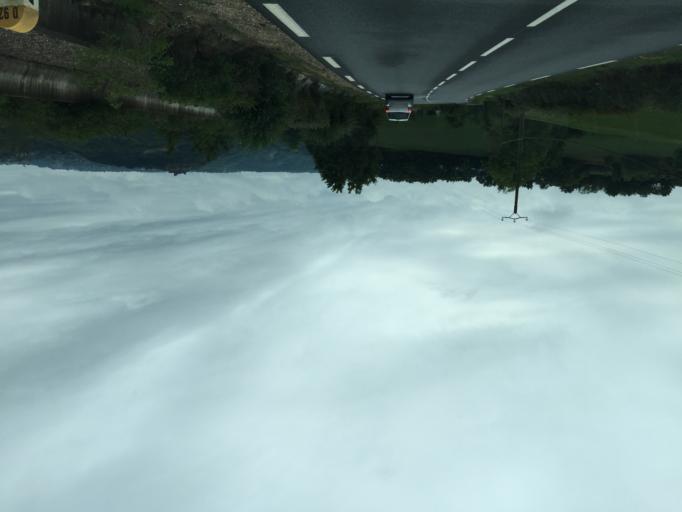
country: FR
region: Midi-Pyrenees
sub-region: Departement de l'Aveyron
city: Espalion
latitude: 44.5354
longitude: 2.7691
